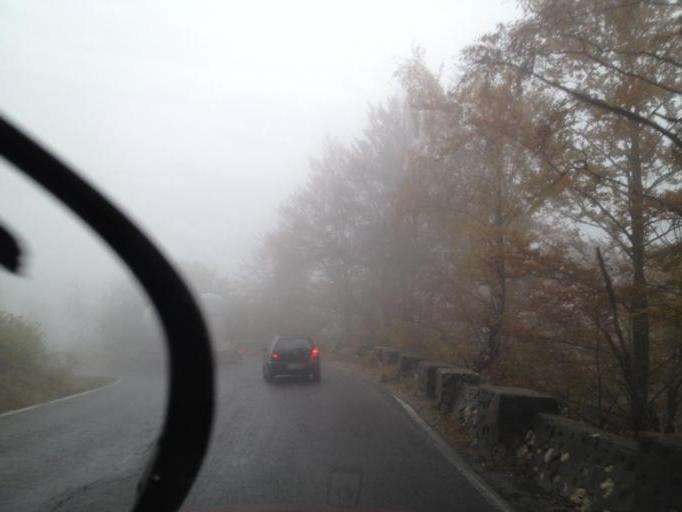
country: RO
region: Arges
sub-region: Comuna Dambovicioara
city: Dambovicioara
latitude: 45.4285
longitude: 25.2507
